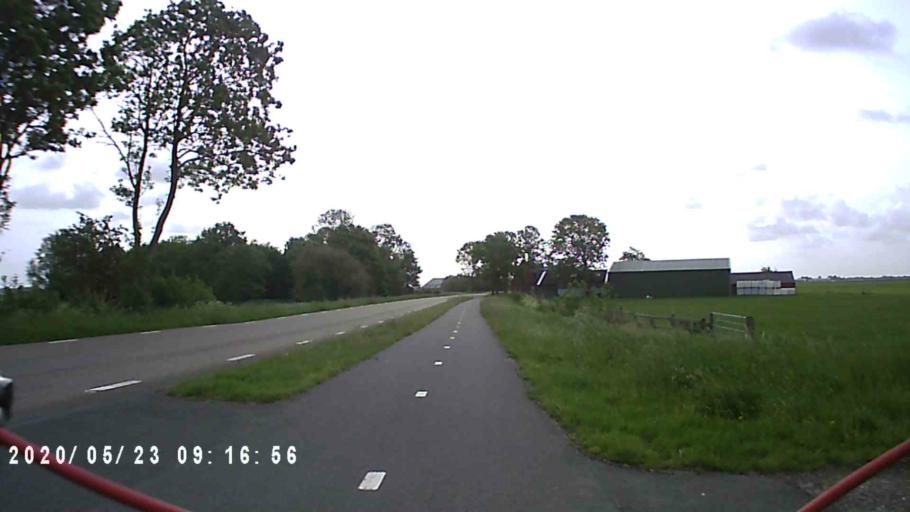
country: NL
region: Groningen
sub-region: Gemeente Bedum
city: Bedum
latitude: 53.3016
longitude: 6.6536
